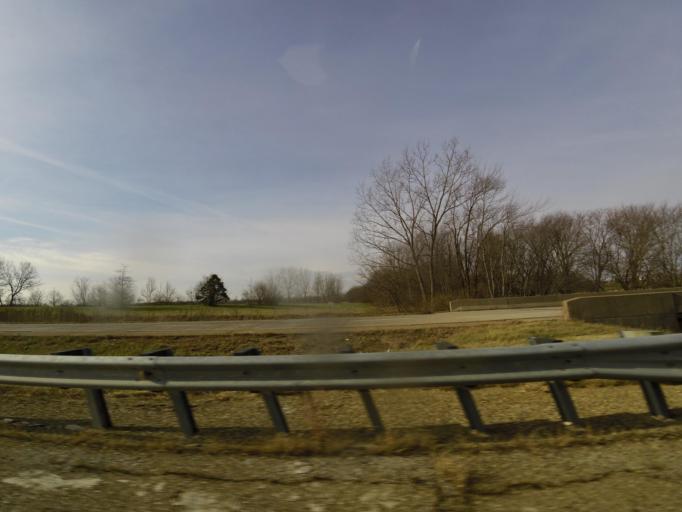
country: US
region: Illinois
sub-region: McLean County
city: Heyworth
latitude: 40.3247
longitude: -88.9894
